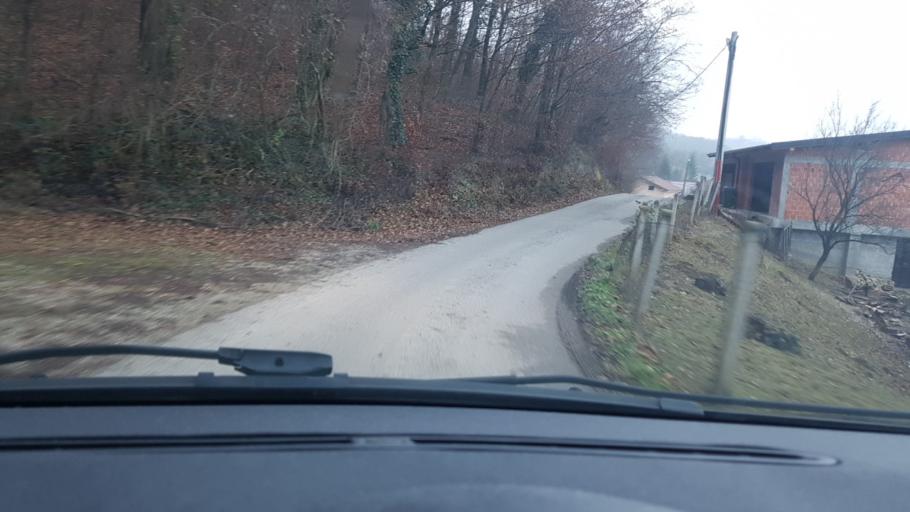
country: HR
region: Krapinsko-Zagorska
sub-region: Grad Krapina
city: Krapina
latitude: 46.1394
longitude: 15.8680
